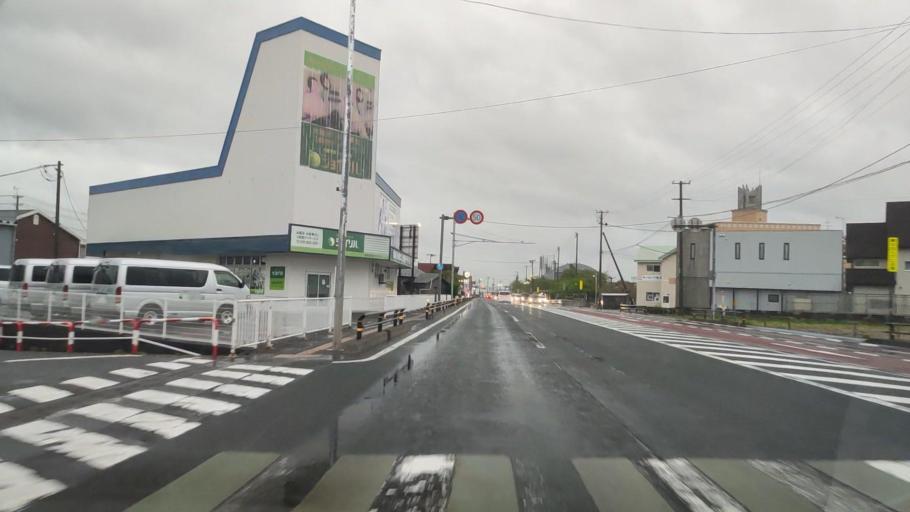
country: JP
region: Akita
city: Akita
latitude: 39.6931
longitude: 140.1212
